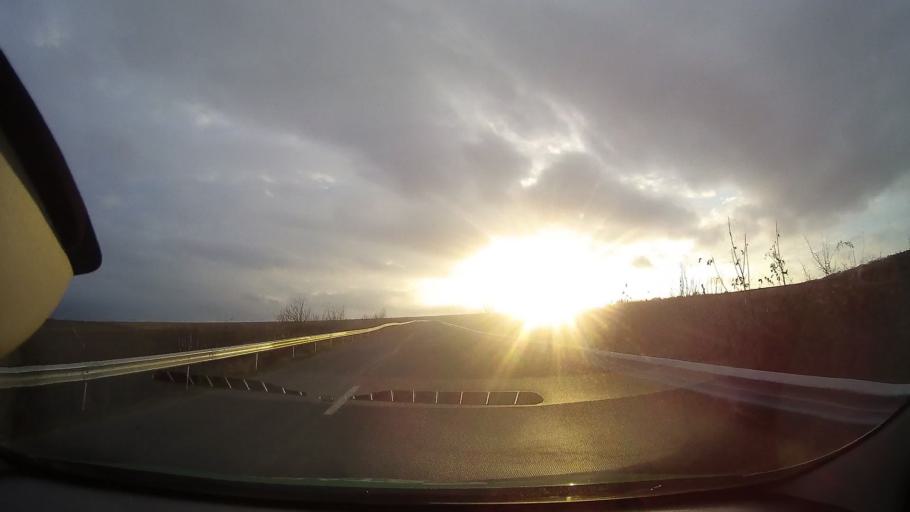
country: RO
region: Constanta
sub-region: Comuna Adamclisi
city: Adamclisi
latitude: 44.0371
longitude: 27.9397
